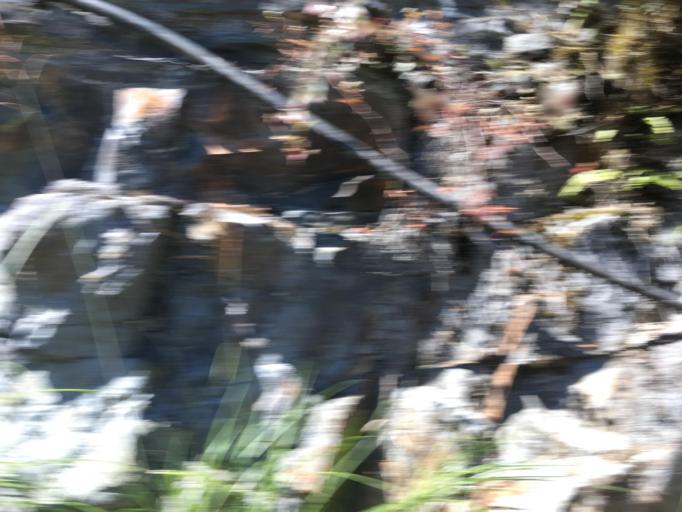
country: TW
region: Taiwan
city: Daxi
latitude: 24.5844
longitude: 121.4124
